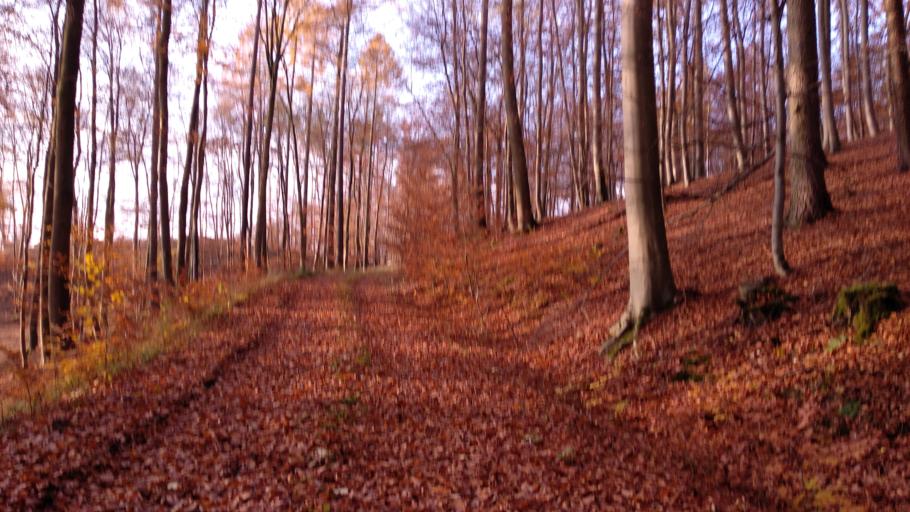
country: DE
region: North Rhine-Westphalia
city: Beverungen
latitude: 51.6562
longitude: 9.3294
